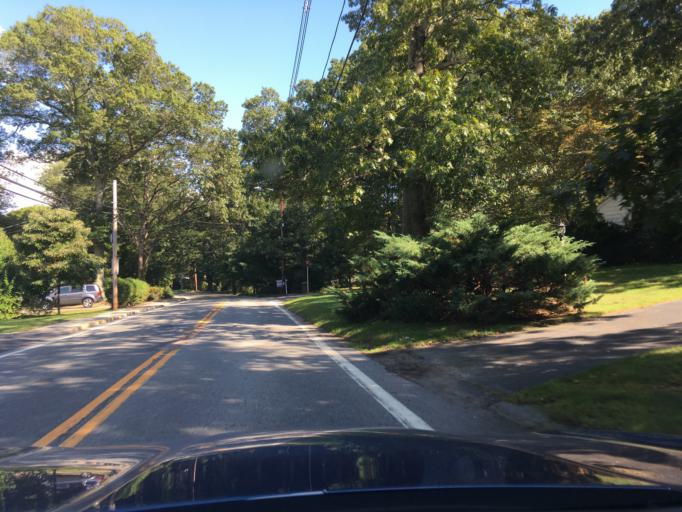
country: US
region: Rhode Island
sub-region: Bristol County
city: Barrington
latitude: 41.7287
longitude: -71.3128
